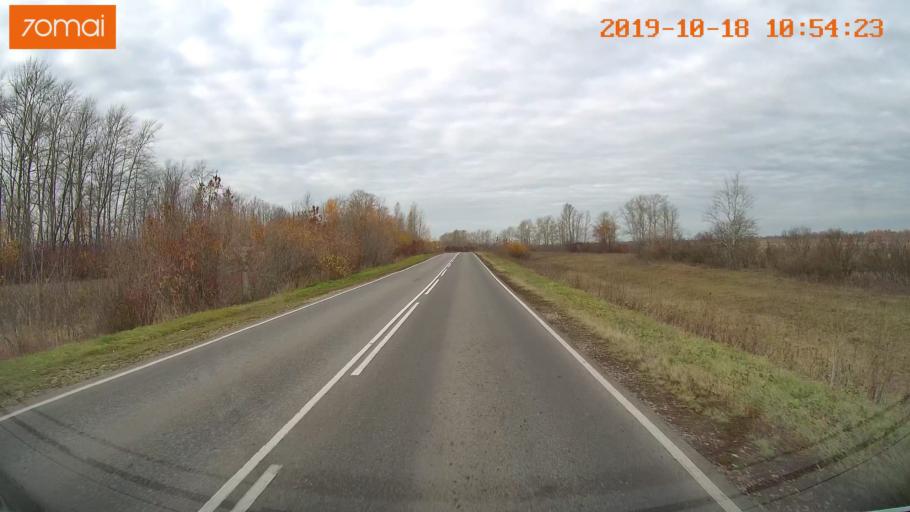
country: RU
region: Tula
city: Yepifan'
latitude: 53.7886
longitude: 38.6189
